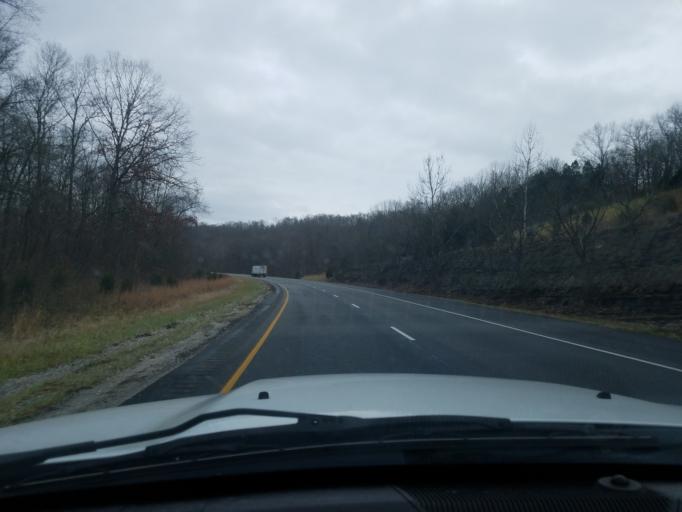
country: US
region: Indiana
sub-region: Crawford County
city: English
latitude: 38.2387
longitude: -86.4060
